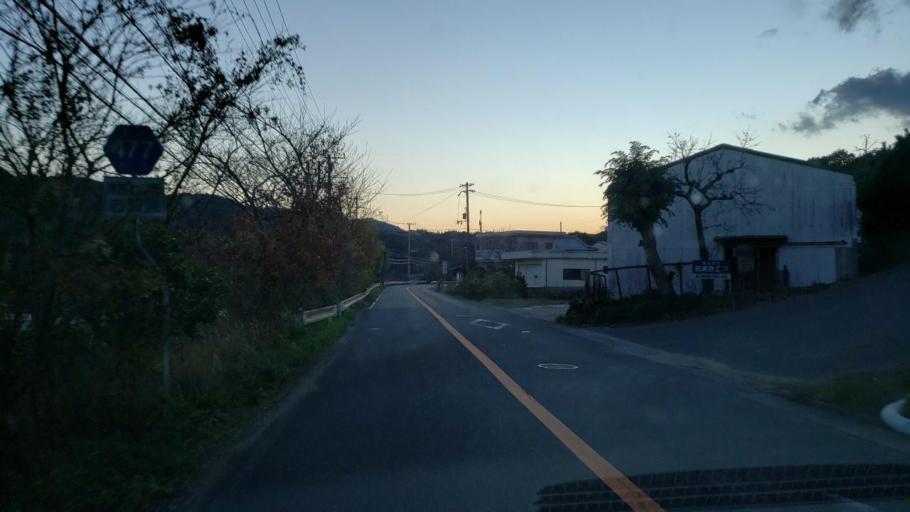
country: JP
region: Hyogo
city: Fukura
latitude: 34.2921
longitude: 134.7220
